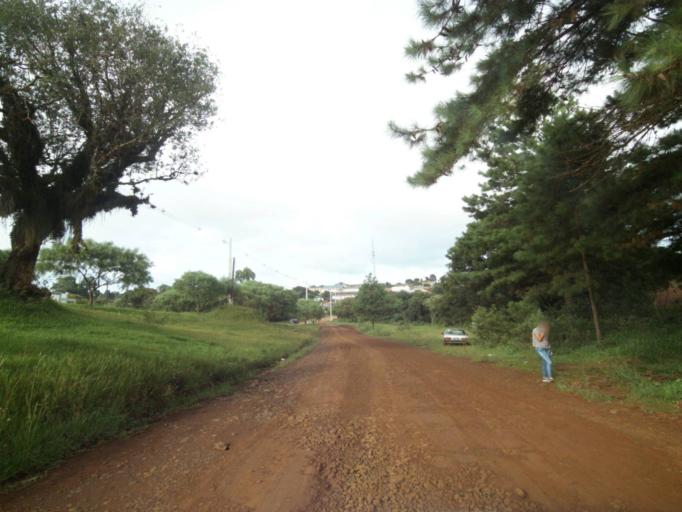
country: BR
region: Parana
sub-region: Pitanga
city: Pitanga
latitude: -24.9397
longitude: -51.8664
